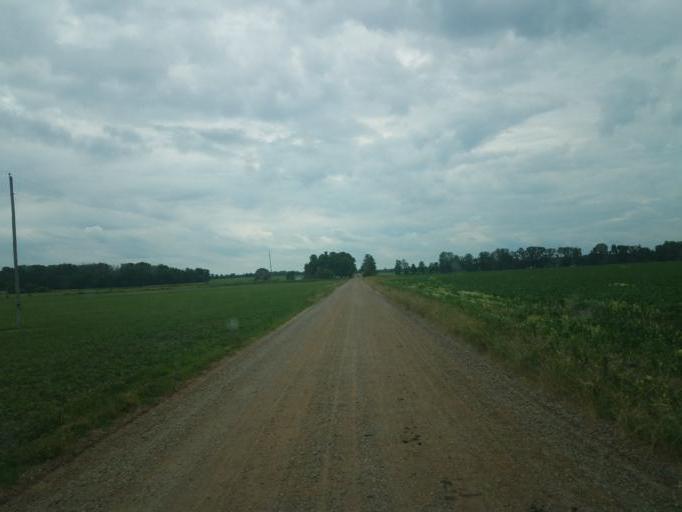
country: US
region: Michigan
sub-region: Barry County
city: Nashville
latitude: 42.6672
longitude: -84.9754
